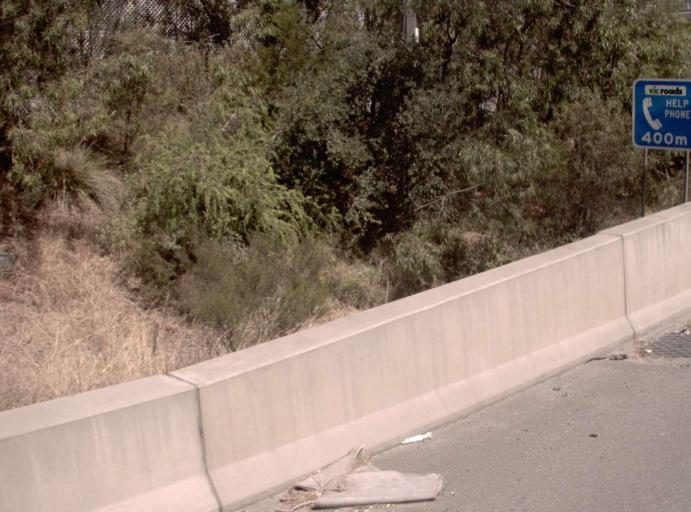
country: AU
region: Victoria
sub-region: Monash
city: Chadstone
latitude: -37.8802
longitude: 145.0859
